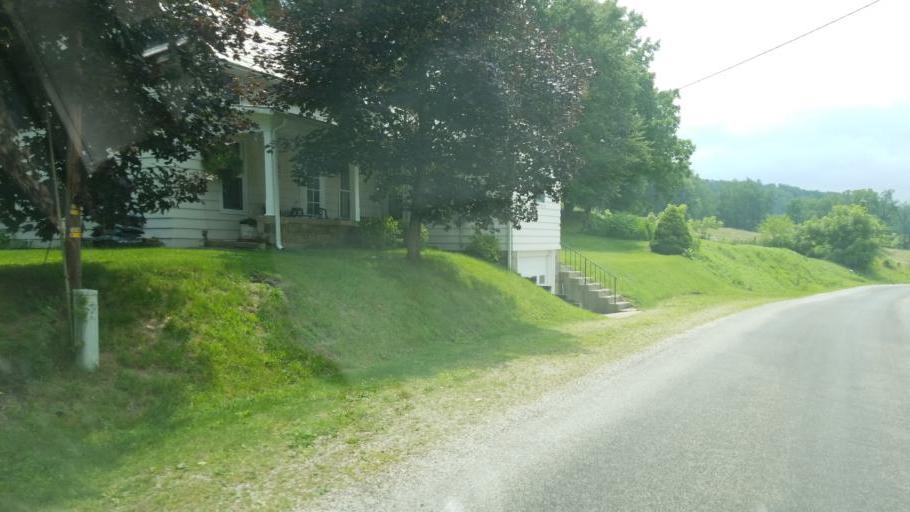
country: US
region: Ohio
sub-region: Licking County
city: Utica
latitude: 40.1756
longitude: -82.4325
